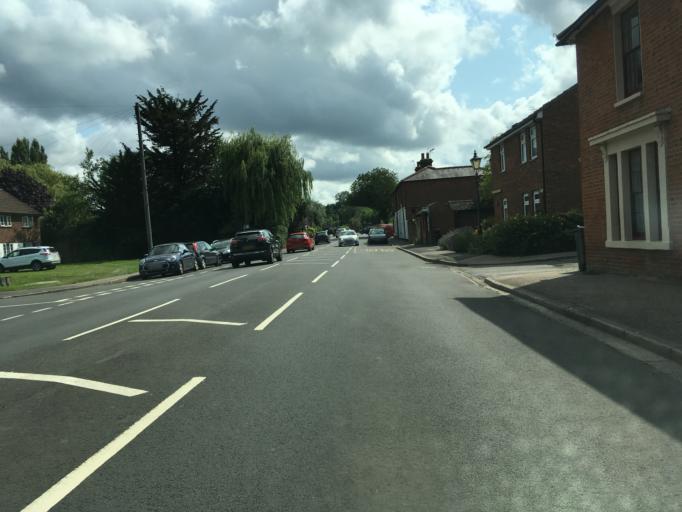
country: GB
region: England
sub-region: Kent
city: Headcorn
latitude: 51.1156
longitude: 0.6438
